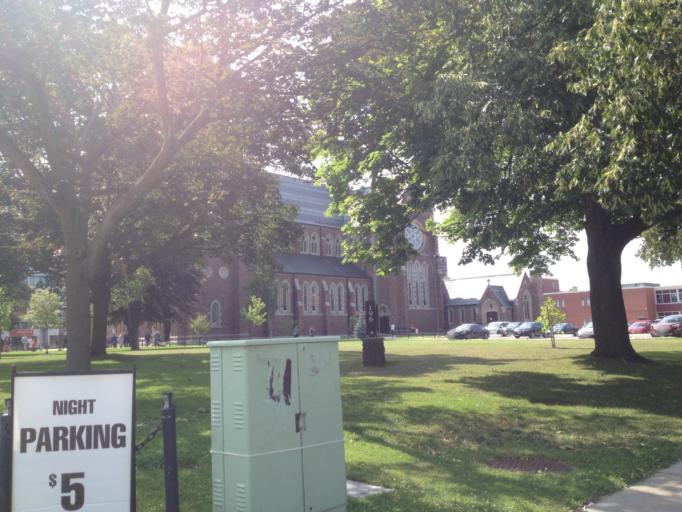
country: CA
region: Ontario
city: London
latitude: 42.9869
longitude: -81.2490
